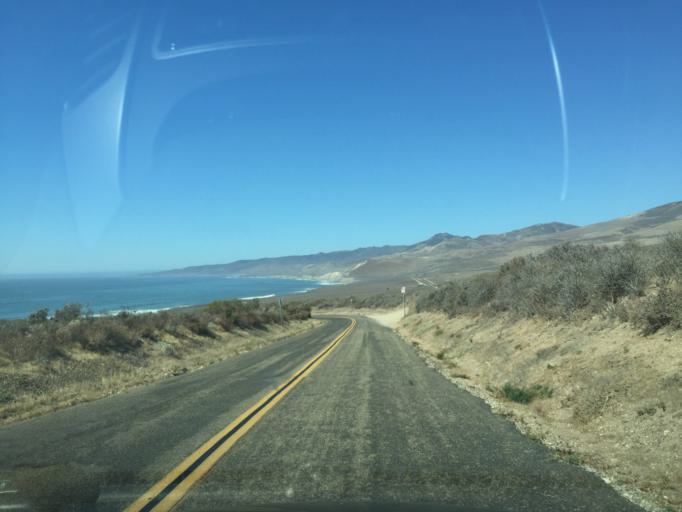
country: US
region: California
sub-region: Santa Barbara County
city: Lompoc
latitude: 34.5099
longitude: -120.4964
